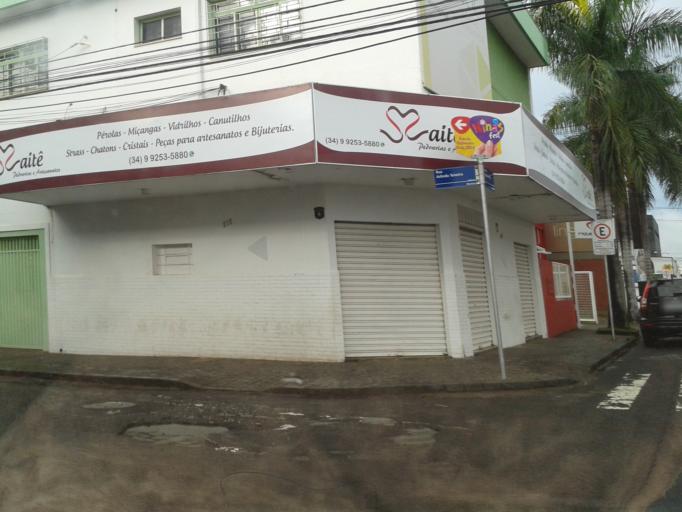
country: BR
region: Minas Gerais
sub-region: Uberlandia
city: Uberlandia
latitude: -18.9110
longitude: -48.2807
